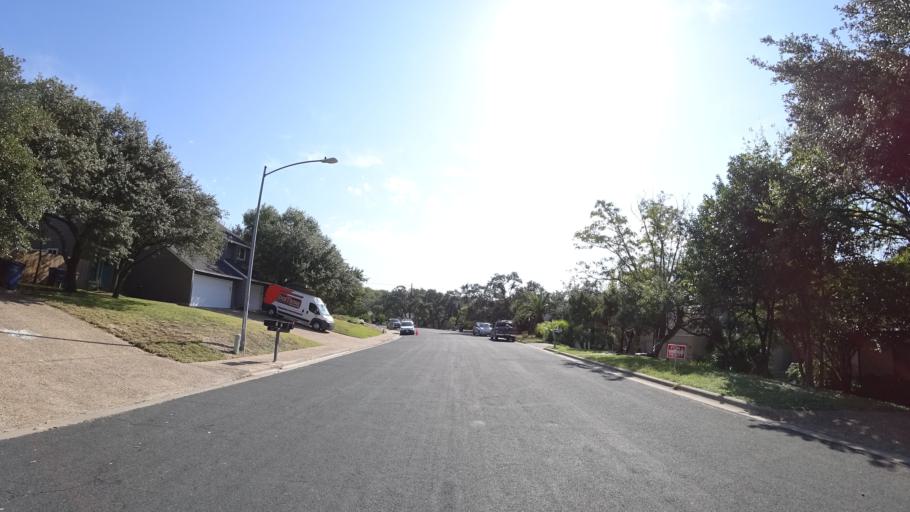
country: US
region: Texas
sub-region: Travis County
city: West Lake Hills
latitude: 30.3517
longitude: -97.7594
